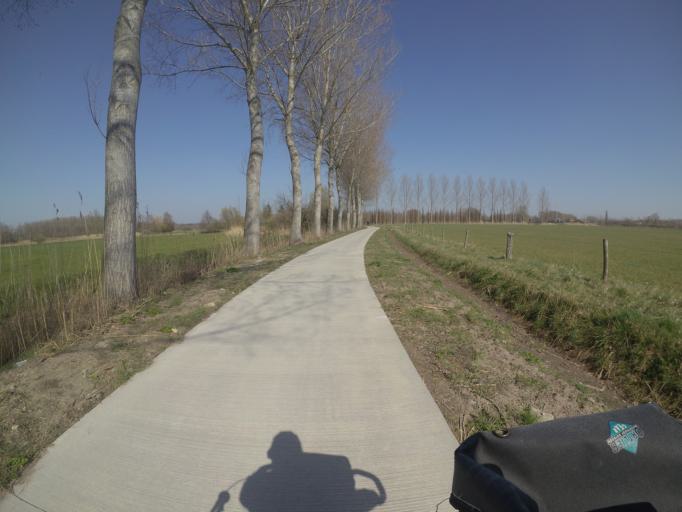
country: NL
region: North Brabant
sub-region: Gemeente Schijndel
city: Schijndel
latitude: 51.5783
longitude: 5.3951
